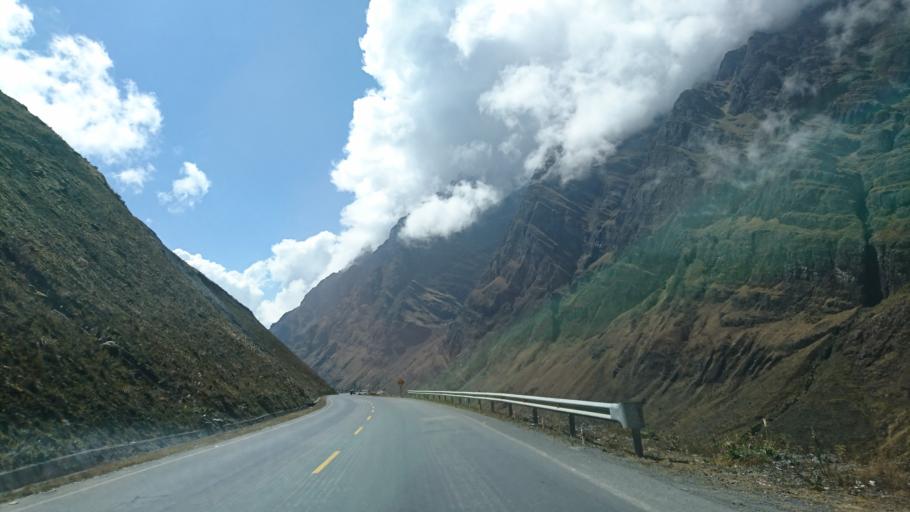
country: BO
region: La Paz
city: Coroico
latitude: -16.3287
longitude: -67.9505
